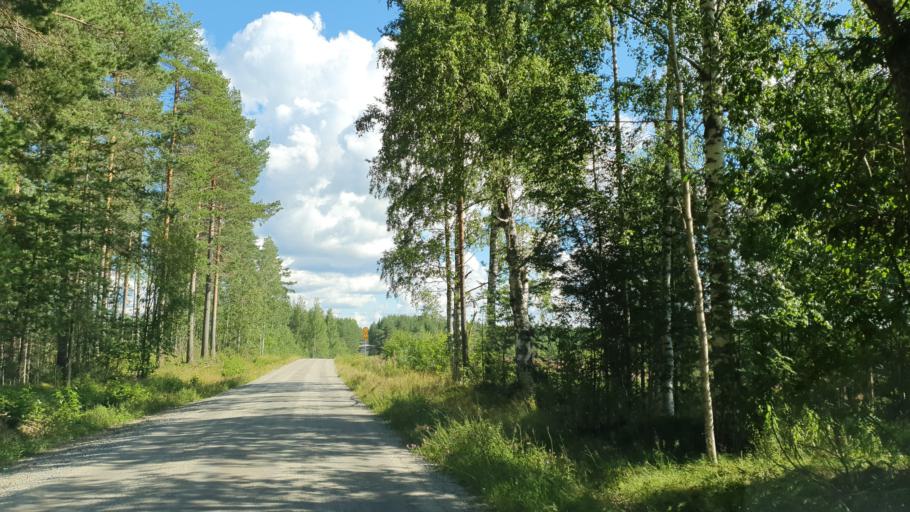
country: FI
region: Kainuu
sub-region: Kehys-Kainuu
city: Kuhmo
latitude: 64.1099
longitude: 29.3805
